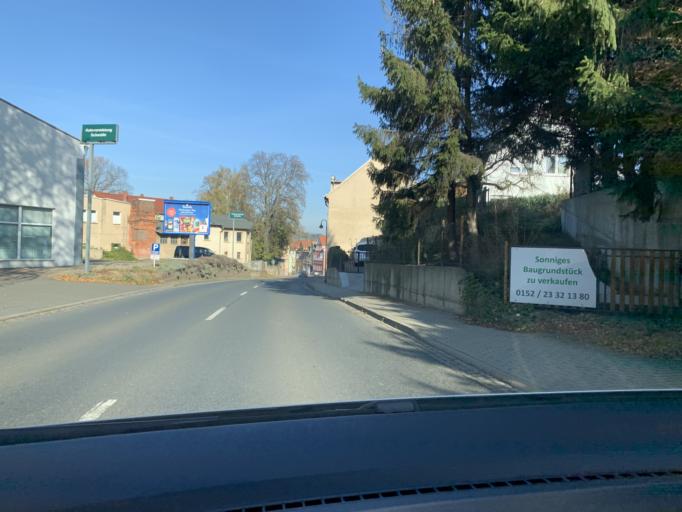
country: DE
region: Thuringia
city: Schmolln
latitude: 50.8913
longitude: 12.3505
